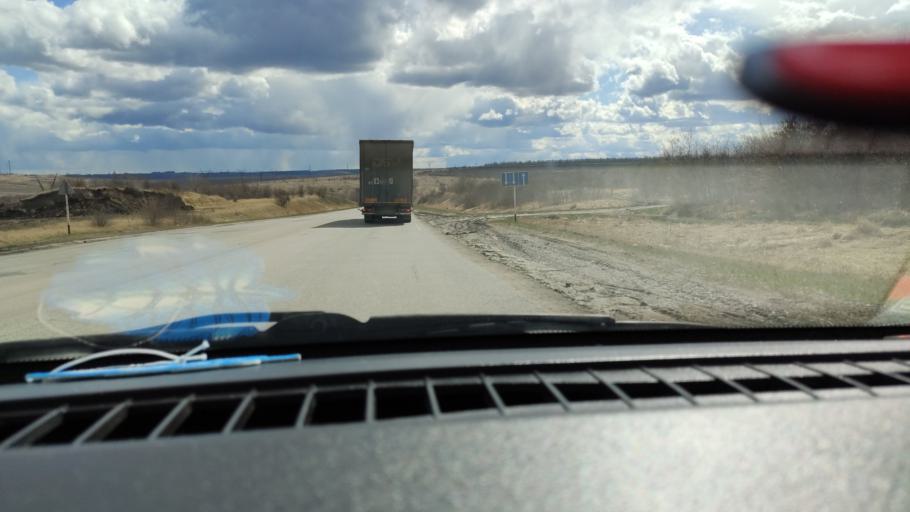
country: RU
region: Samara
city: Varlamovo
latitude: 53.0991
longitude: 48.3562
